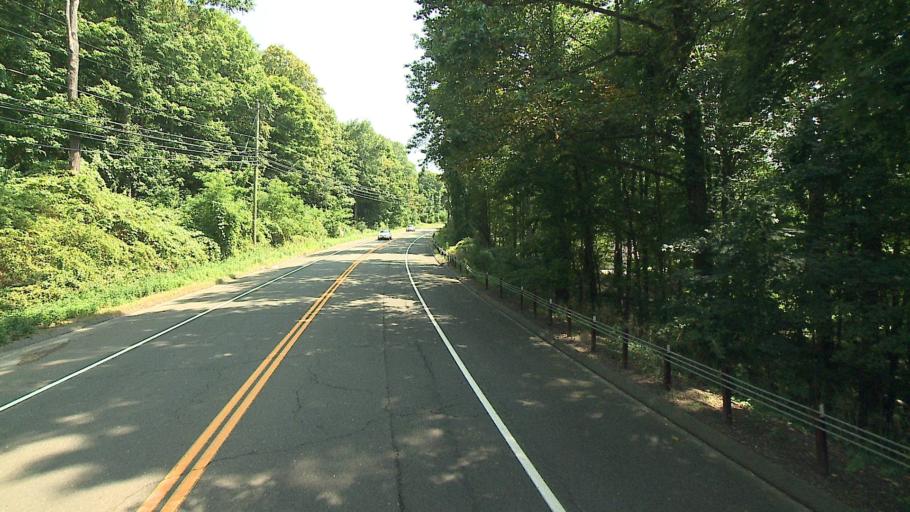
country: US
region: Connecticut
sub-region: Fairfield County
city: Georgetown
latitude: 41.2529
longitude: -73.4208
